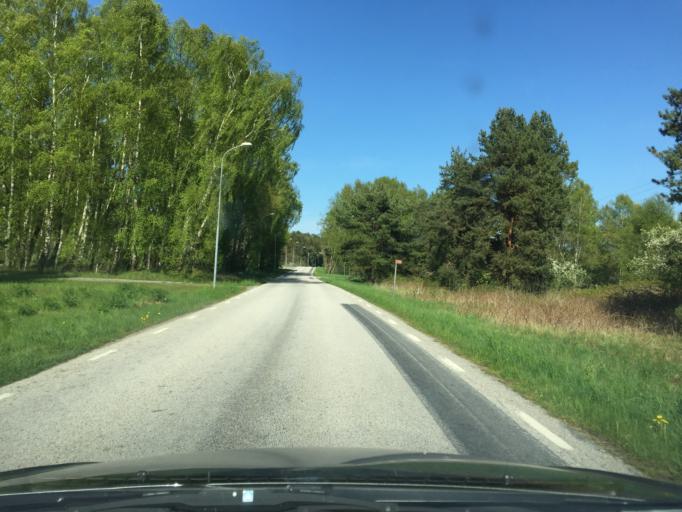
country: SE
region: Skane
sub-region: Sjobo Kommun
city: Blentarp
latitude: 55.5773
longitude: 13.5928
